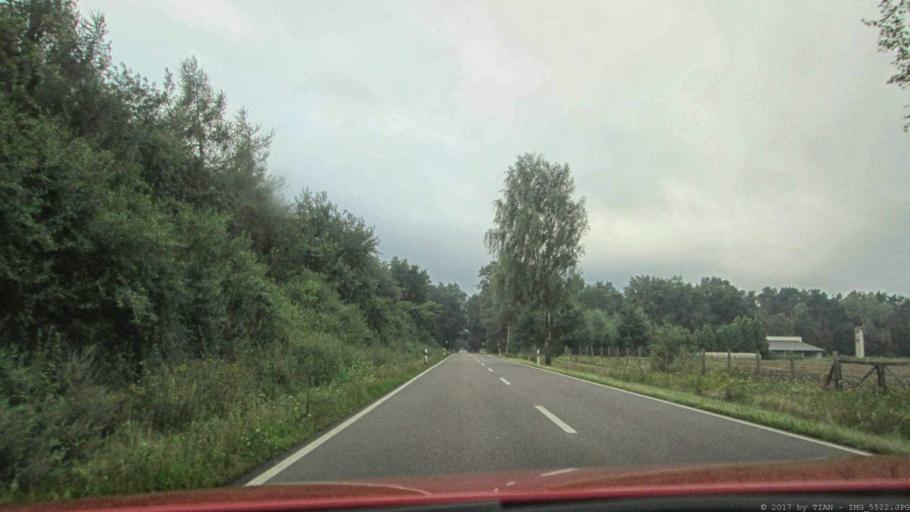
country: DE
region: Lower Saxony
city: Tulau
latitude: 52.6179
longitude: 10.8129
